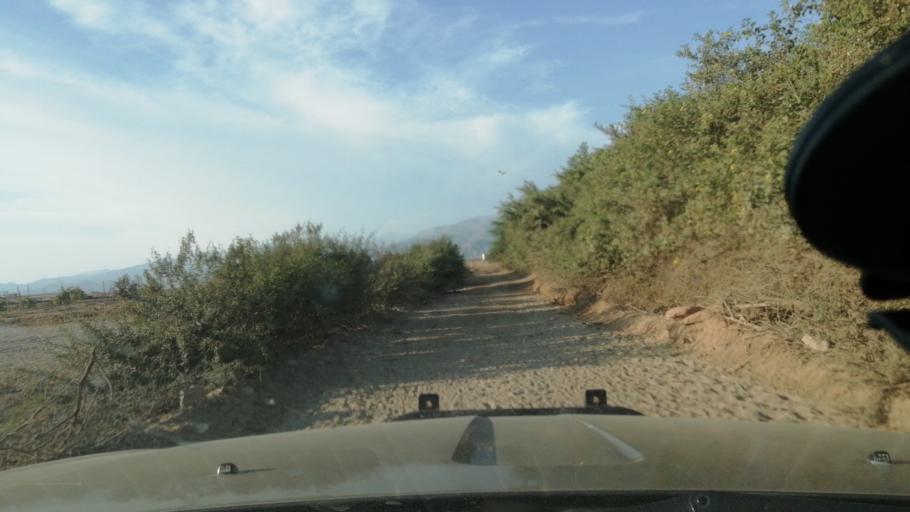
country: PE
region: Ica
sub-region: Provincia de Chincha
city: San Pedro
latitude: -13.3417
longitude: -76.1587
